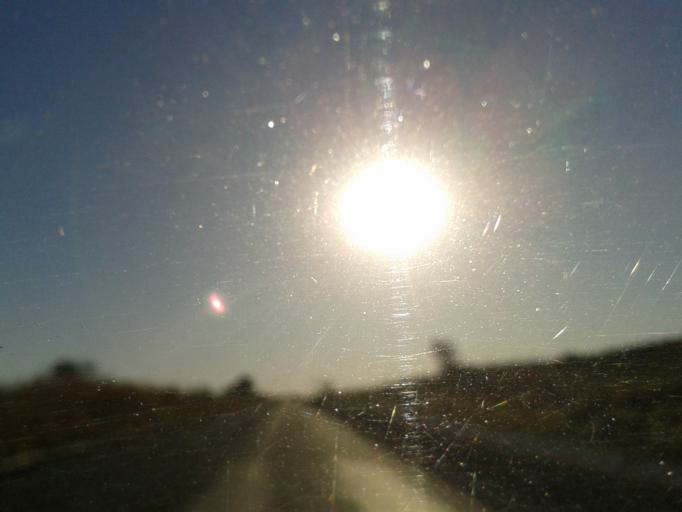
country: BR
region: Minas Gerais
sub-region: Santa Vitoria
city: Santa Vitoria
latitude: -19.1199
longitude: -50.3016
